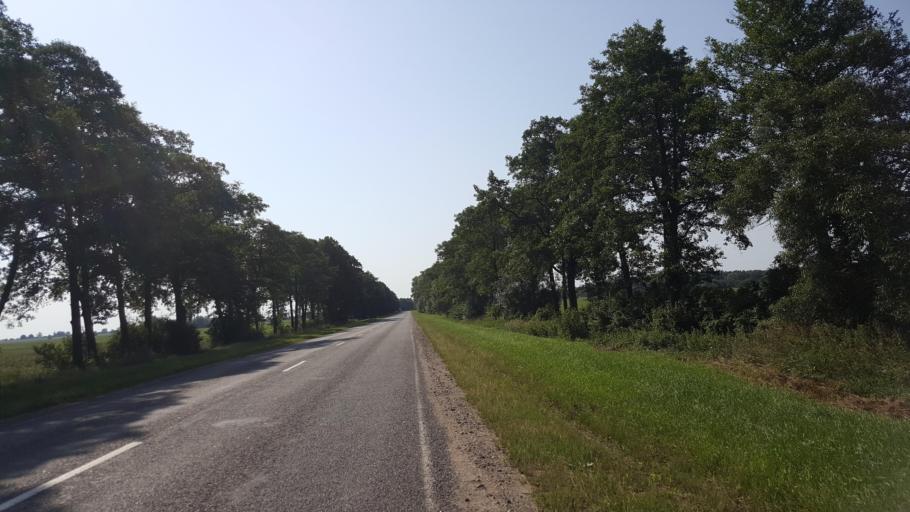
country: BY
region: Brest
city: Zhabinka
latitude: 52.3046
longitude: 23.9284
